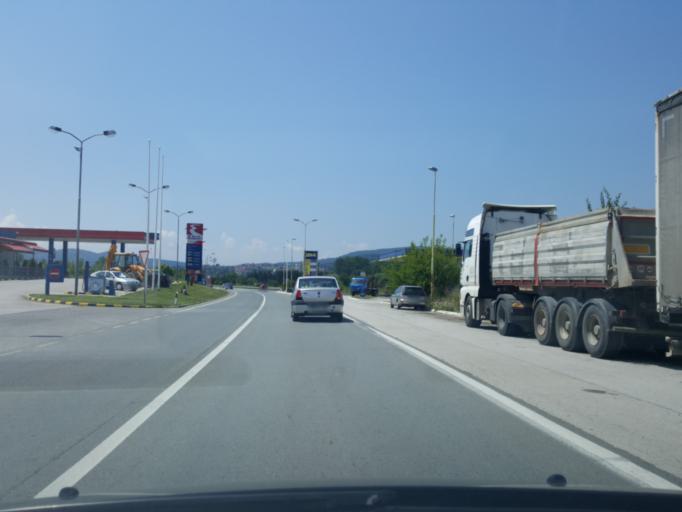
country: RS
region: Central Serbia
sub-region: Moravicki Okrug
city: Gornji Milanovac
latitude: 44.0325
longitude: 20.4750
